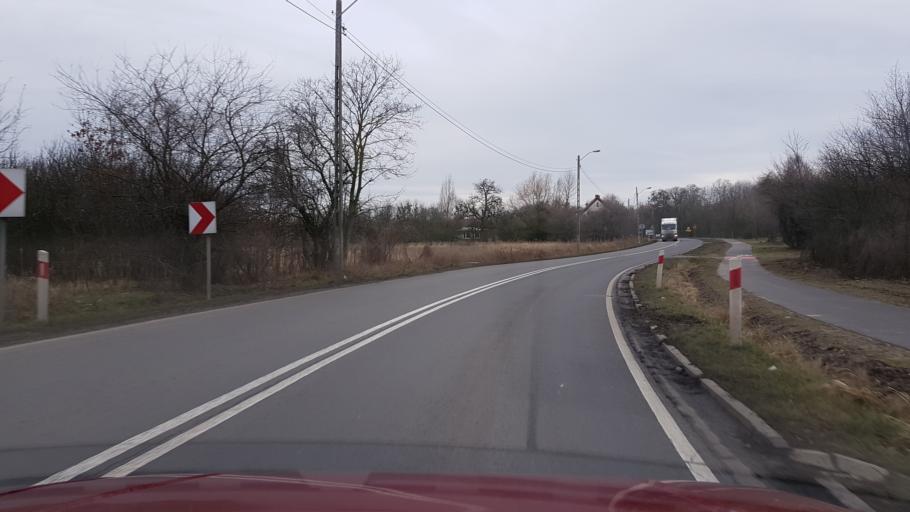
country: PL
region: West Pomeranian Voivodeship
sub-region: Powiat policki
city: Police
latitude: 53.5877
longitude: 14.5476
